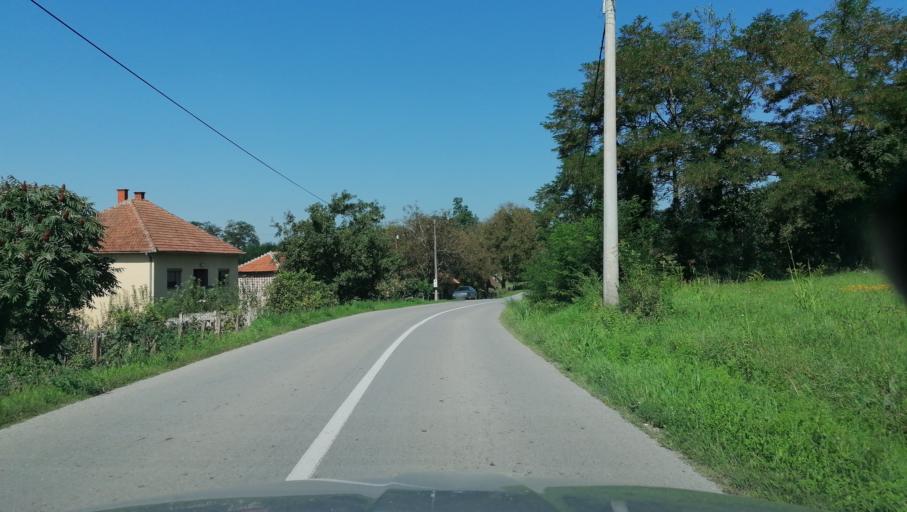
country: RS
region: Central Serbia
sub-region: Raski Okrug
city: Vrnjacka Banja
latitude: 43.6799
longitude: 20.8937
